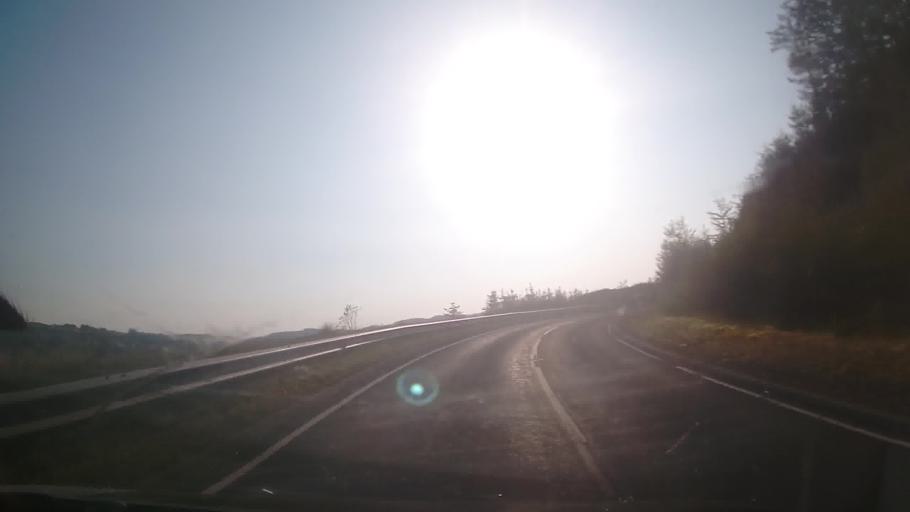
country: GB
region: Wales
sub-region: County of Ceredigion
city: Lledrod
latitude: 52.3426
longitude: -3.8394
